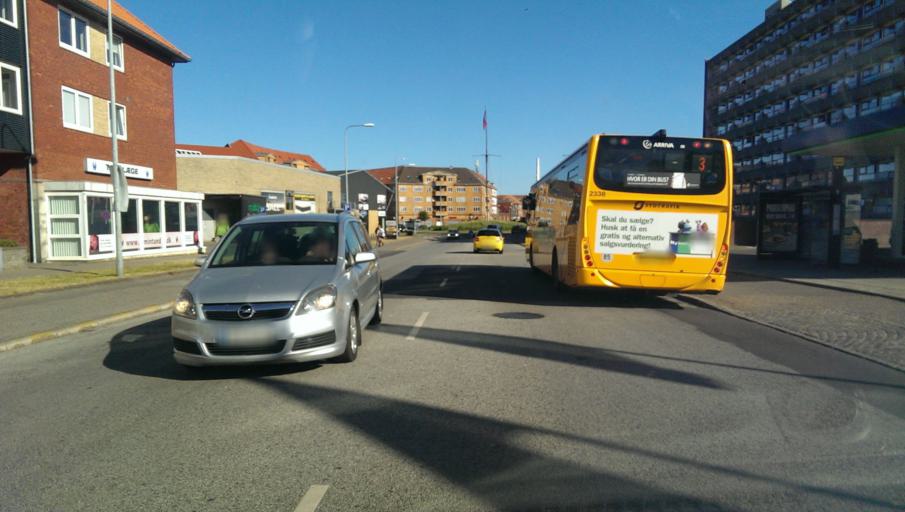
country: DK
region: South Denmark
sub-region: Esbjerg Kommune
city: Esbjerg
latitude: 55.4751
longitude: 8.4347
